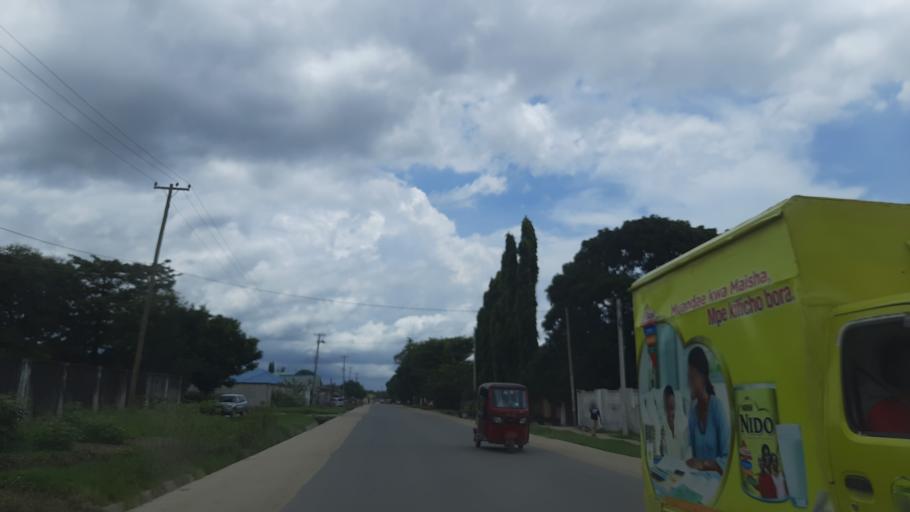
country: TZ
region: Dar es Salaam
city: Magomeni
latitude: -6.7778
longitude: 39.2362
